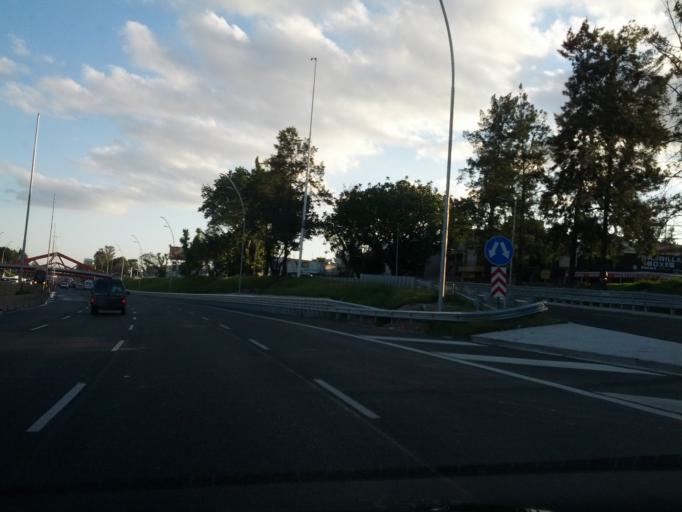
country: AR
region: Buenos Aires
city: Caseros
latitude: -34.6156
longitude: -58.5310
